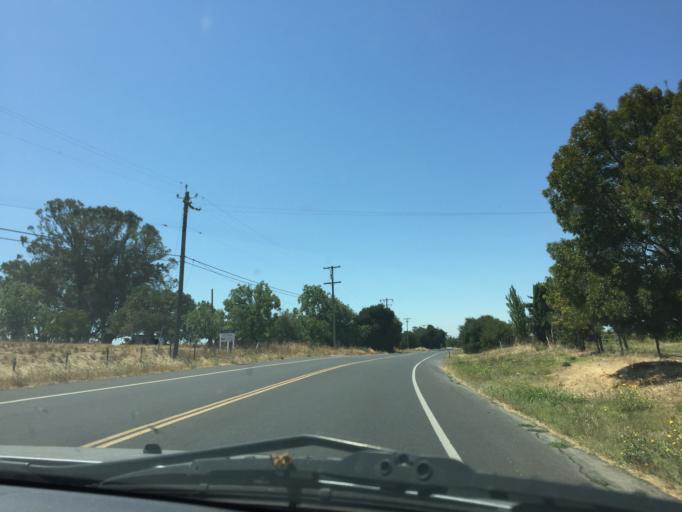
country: US
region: California
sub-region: Napa County
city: Napa
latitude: 38.2606
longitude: -122.3353
